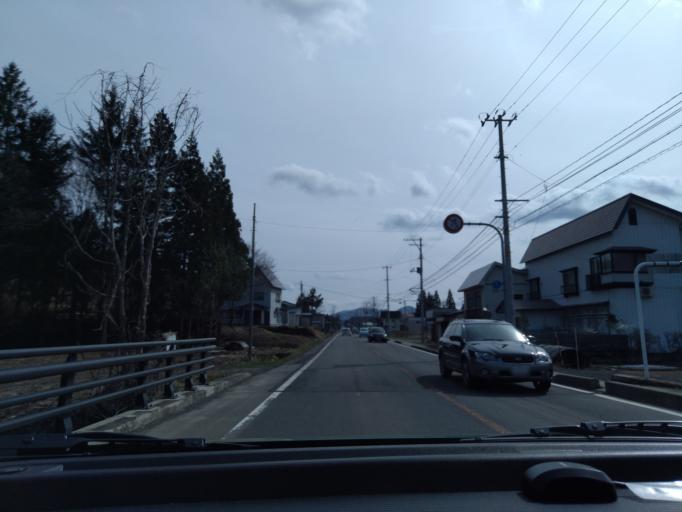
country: JP
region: Akita
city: Yokotemachi
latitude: 39.2994
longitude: 140.7360
